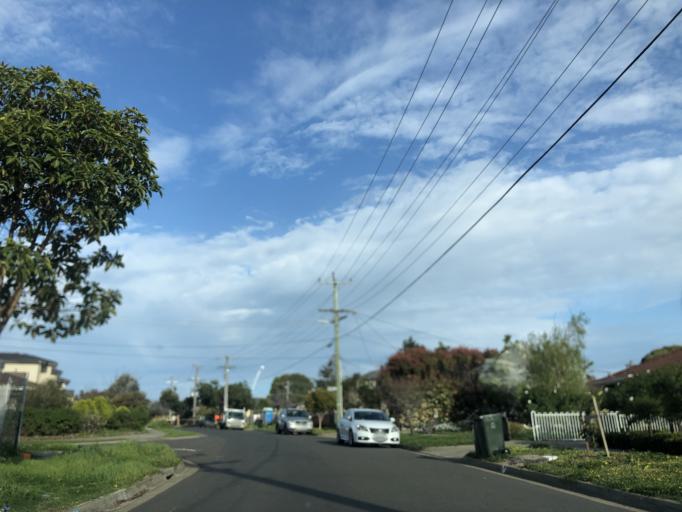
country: AU
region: Victoria
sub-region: Monash
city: Notting Hill
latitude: -37.9020
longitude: 145.1558
